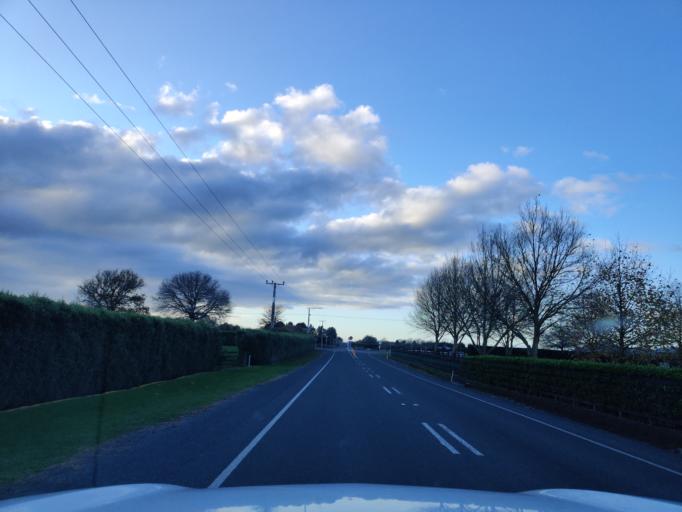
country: NZ
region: Waikato
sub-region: Waipa District
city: Cambridge
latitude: -37.8761
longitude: 175.4389
